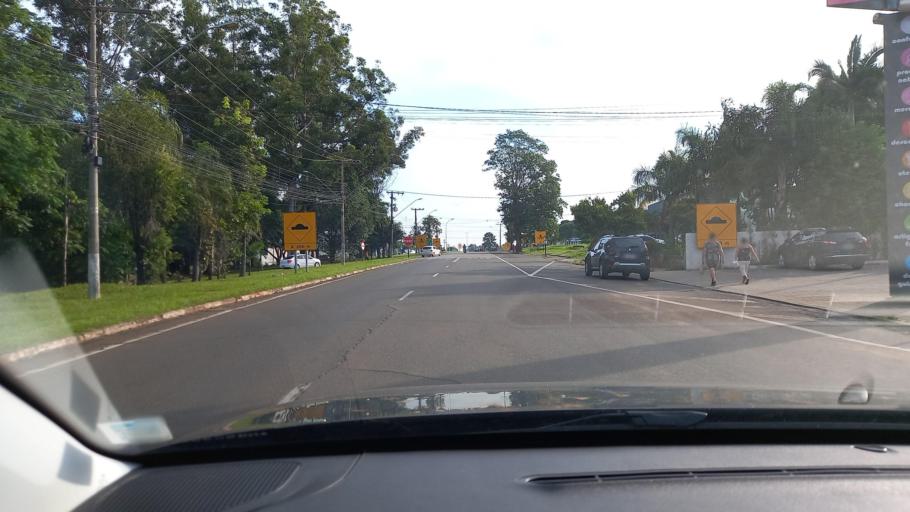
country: BR
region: Sao Paulo
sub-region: Mogi-Mirim
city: Mogi Mirim
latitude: -22.4464
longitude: -46.9770
